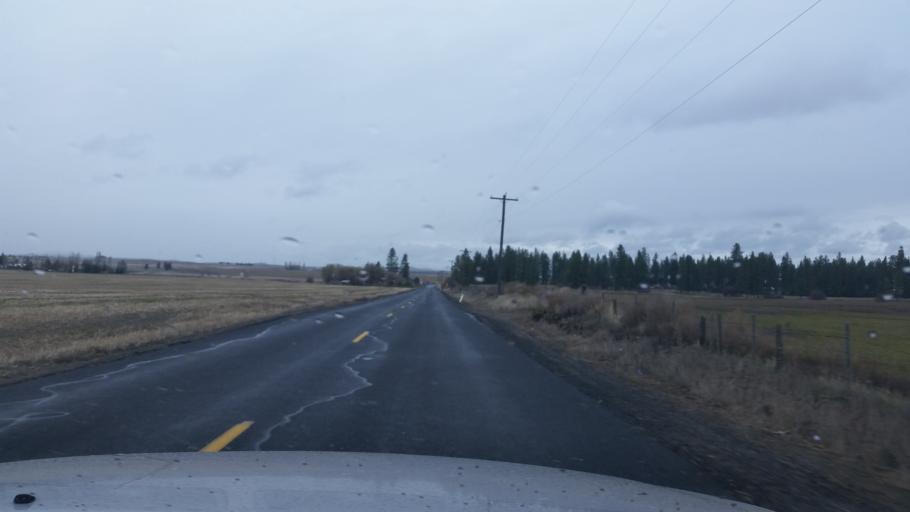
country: US
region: Washington
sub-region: Spokane County
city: Medical Lake
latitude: 47.6078
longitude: -117.7368
